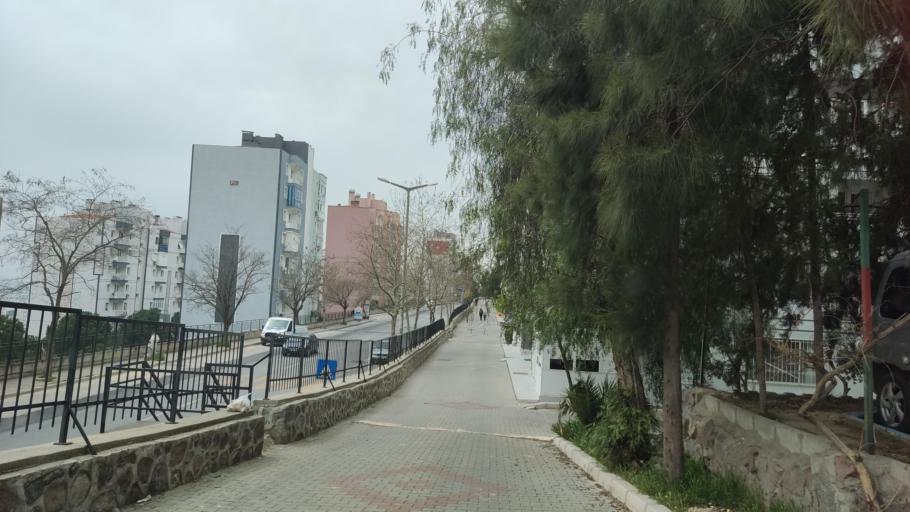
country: TR
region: Izmir
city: Karsiyaka
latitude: 38.5038
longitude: 27.0743
